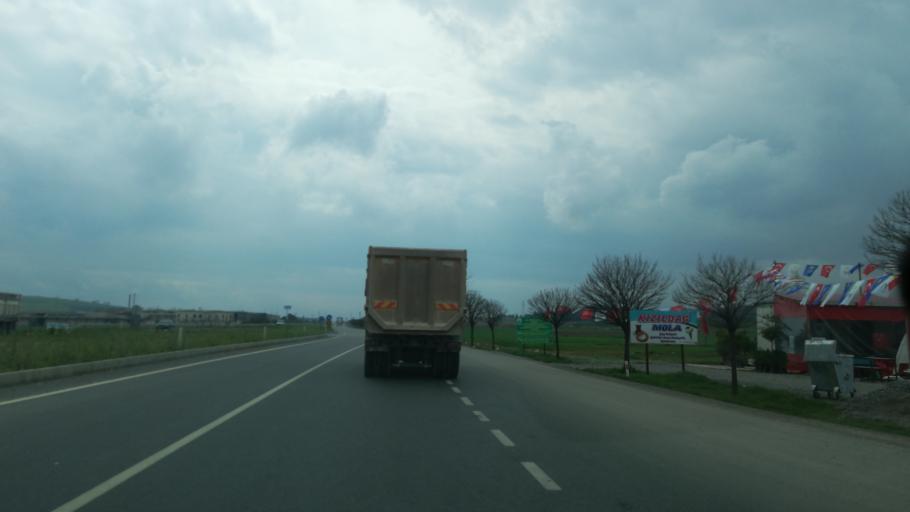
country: TR
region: Kahramanmaras
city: Turkoglu
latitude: 37.4397
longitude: 36.8864
